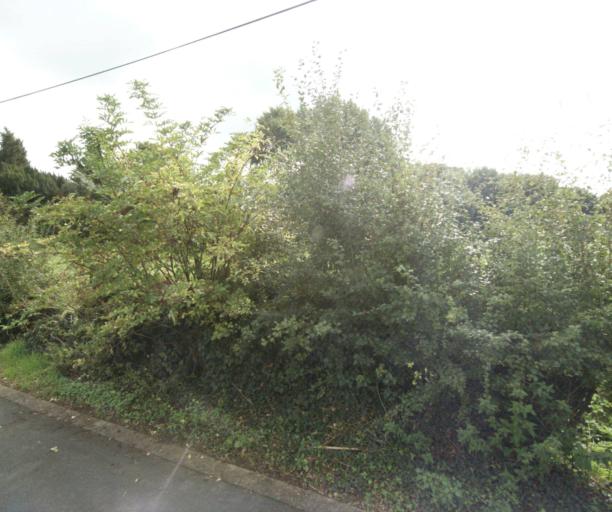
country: FR
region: Nord-Pas-de-Calais
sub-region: Departement du Nord
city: Premesques
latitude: 50.6570
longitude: 2.9490
